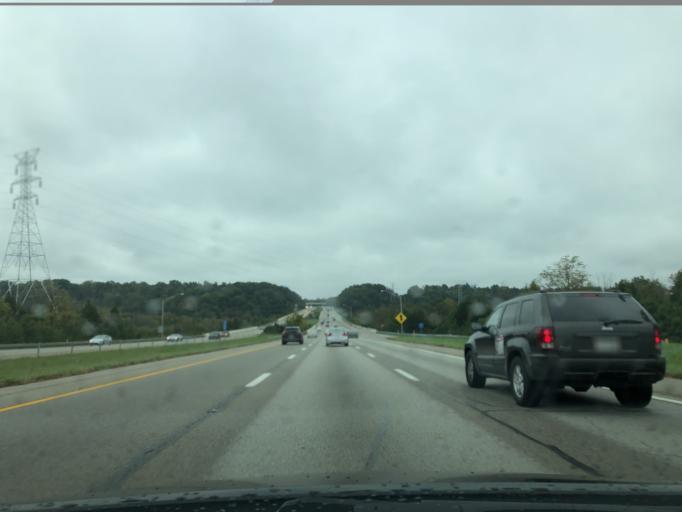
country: US
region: Ohio
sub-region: Hamilton County
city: The Village of Indian Hill
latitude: 39.2426
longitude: -84.3010
